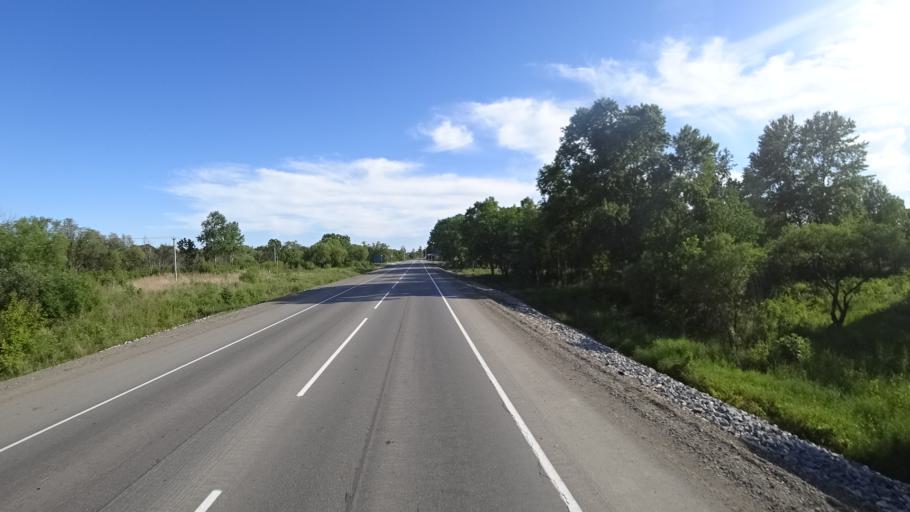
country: RU
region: Khabarovsk Krai
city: Khor
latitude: 47.8586
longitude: 134.9626
